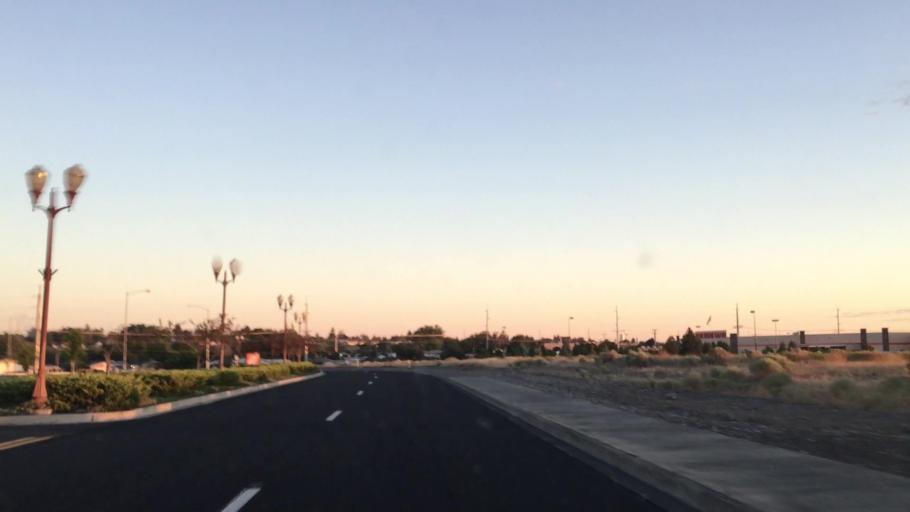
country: US
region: Washington
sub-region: Grant County
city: Moses Lake
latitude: 47.1451
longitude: -119.2906
